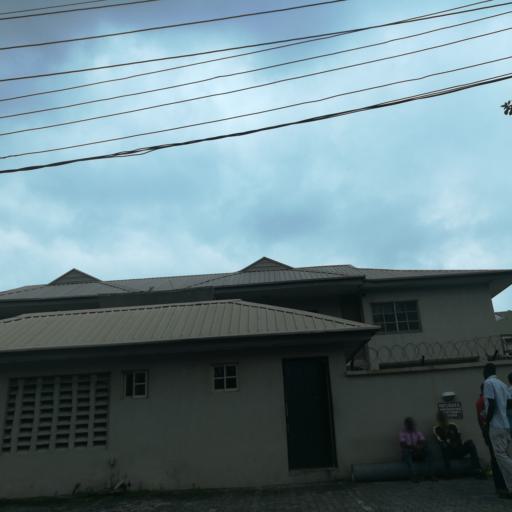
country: NG
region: Lagos
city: Ikoyi
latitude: 6.4407
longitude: 3.4603
